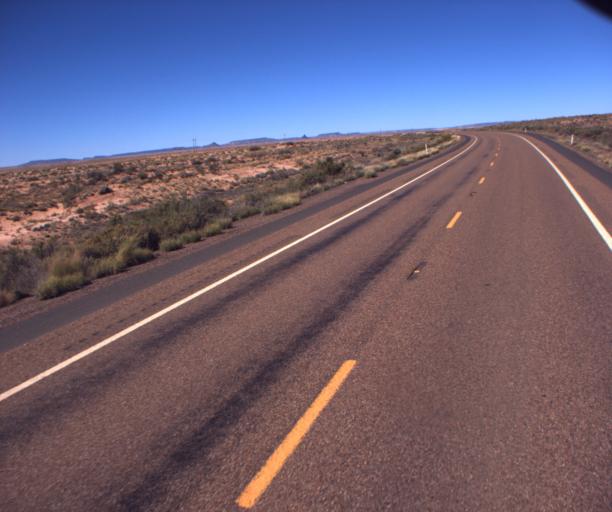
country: US
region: Arizona
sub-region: Navajo County
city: Holbrook
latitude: 35.0582
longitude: -110.0962
